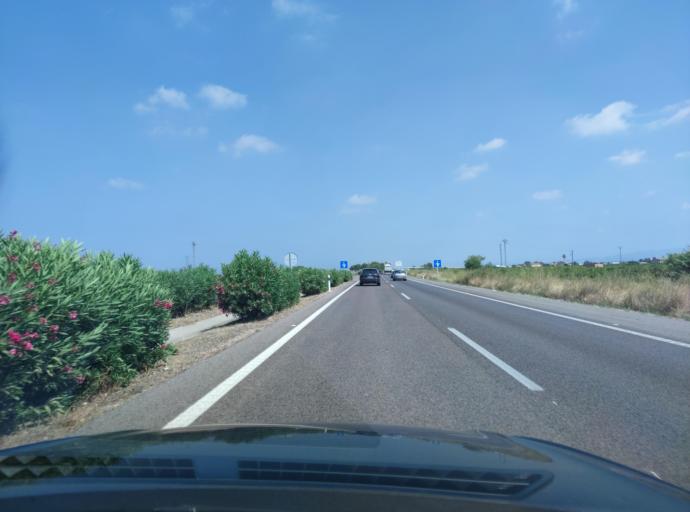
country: ES
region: Valencia
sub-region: Provincia de Castello
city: Alquerias del Nino Perdido
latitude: 39.8895
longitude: -0.1279
